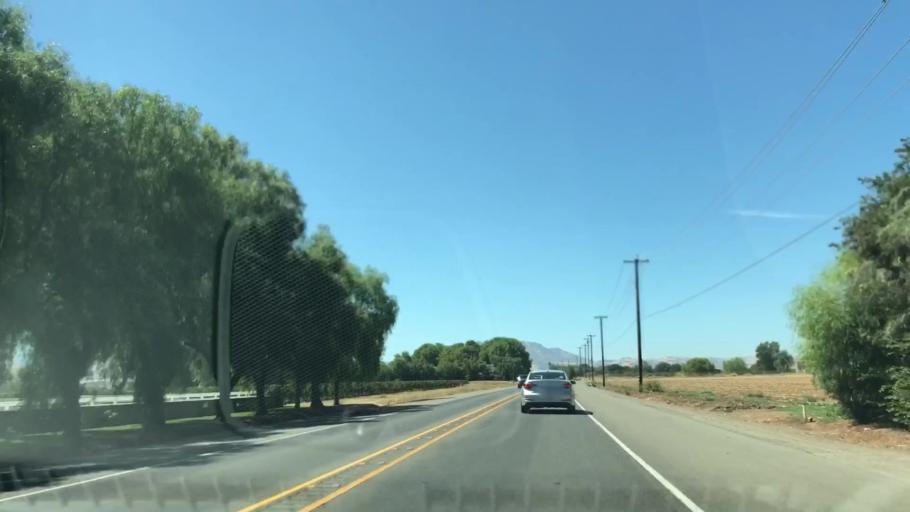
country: US
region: California
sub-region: Contra Costa County
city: Byron
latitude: 37.8965
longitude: -121.6474
